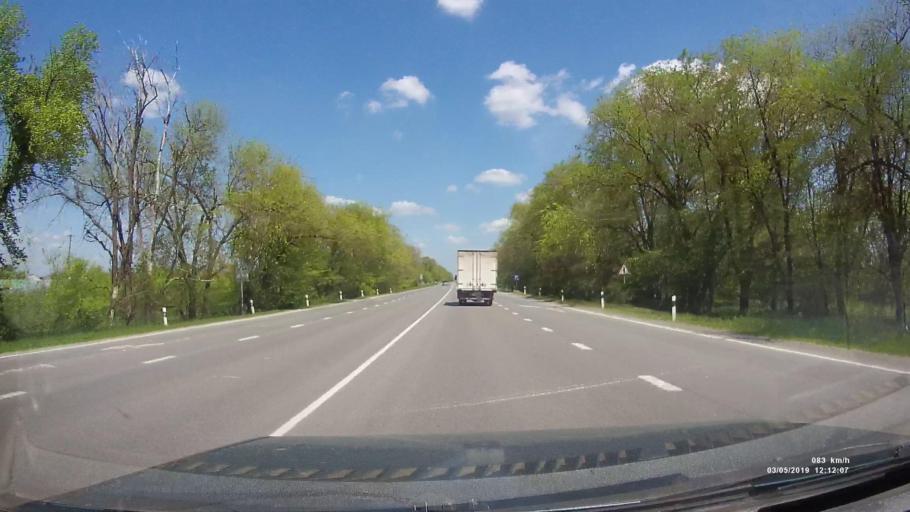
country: RU
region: Rostov
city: Bagayevskaya
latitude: 47.3179
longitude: 40.5439
